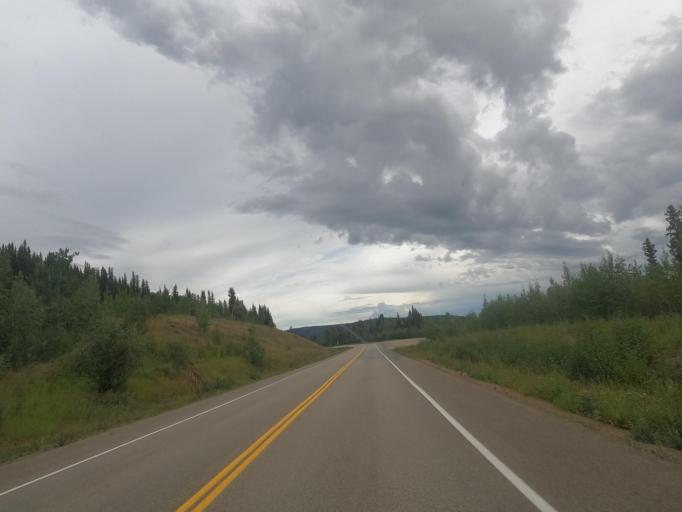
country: US
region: Alaska
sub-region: Southeast Fairbanks Census Area
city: Tok
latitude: 63.0554
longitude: -141.8845
